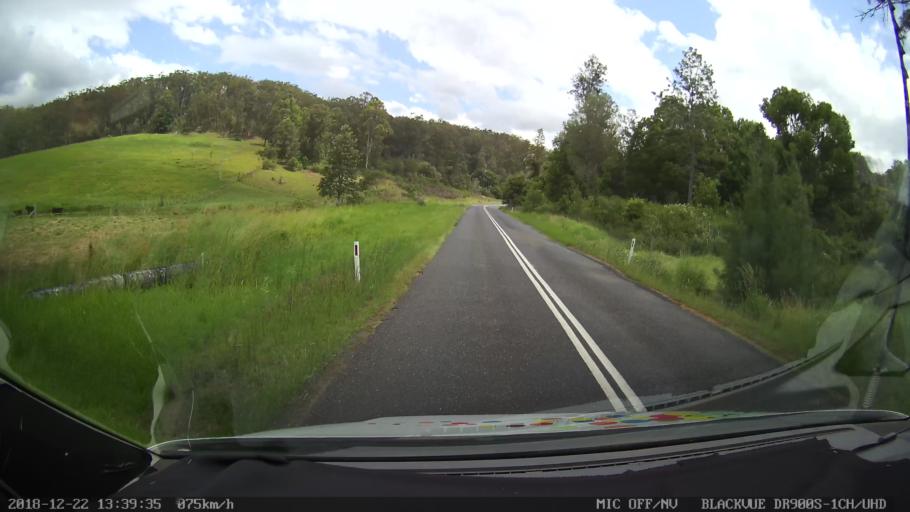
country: AU
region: New South Wales
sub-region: Clarence Valley
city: Coutts Crossing
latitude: -29.9123
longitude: 152.7852
